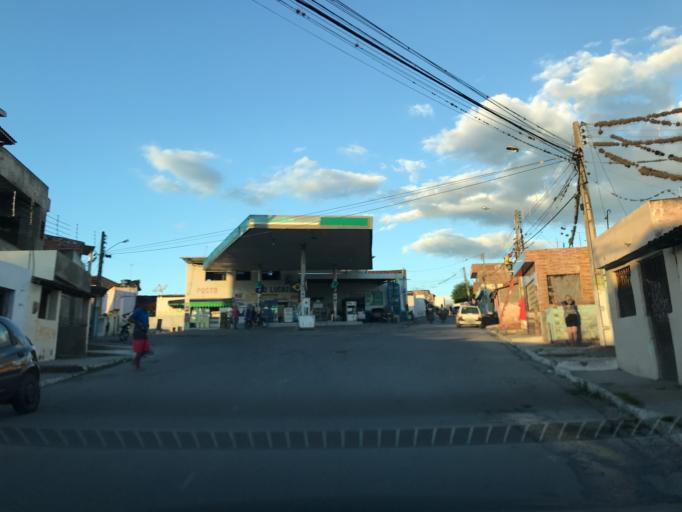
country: BR
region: Pernambuco
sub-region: Bezerros
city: Bezerros
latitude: -8.2379
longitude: -35.7595
